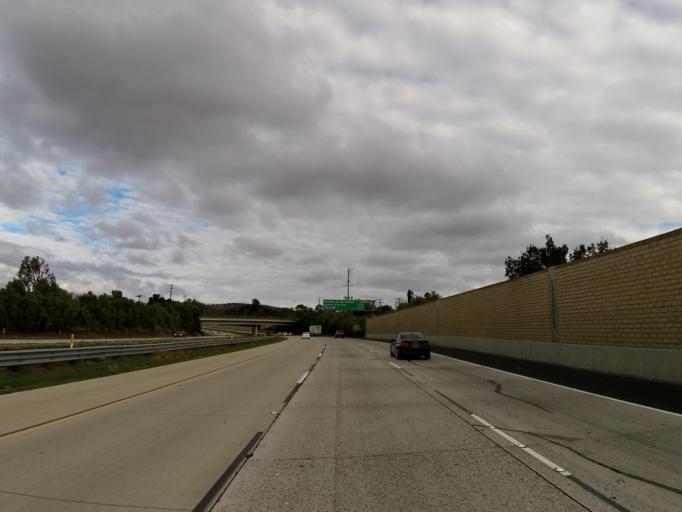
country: US
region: California
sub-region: Ventura County
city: Thousand Oaks
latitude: 34.2039
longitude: -118.8529
